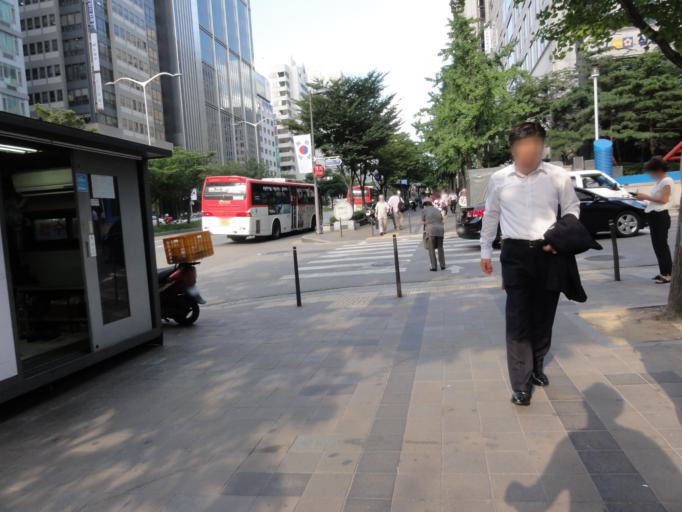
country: KR
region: Seoul
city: Seoul
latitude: 37.4990
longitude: 127.0294
